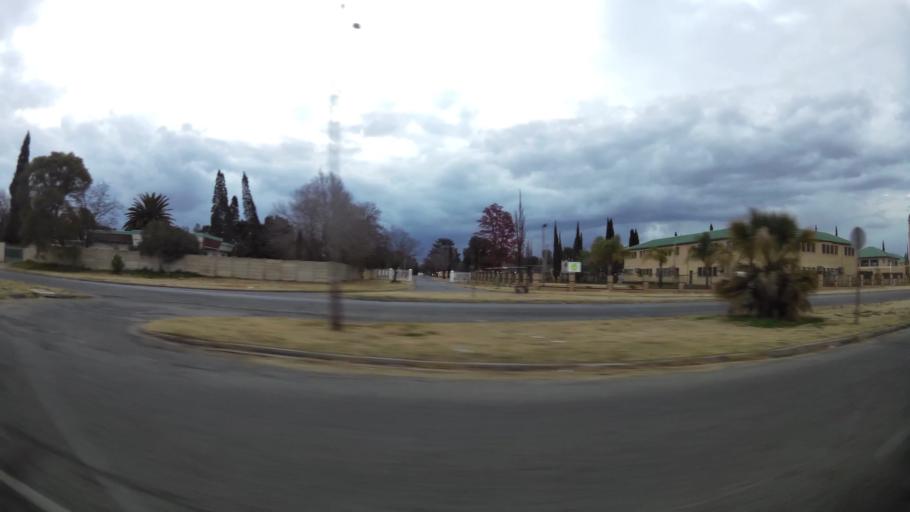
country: ZA
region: Orange Free State
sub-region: Lejweleputswa District Municipality
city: Welkom
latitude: -27.9685
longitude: 26.7358
